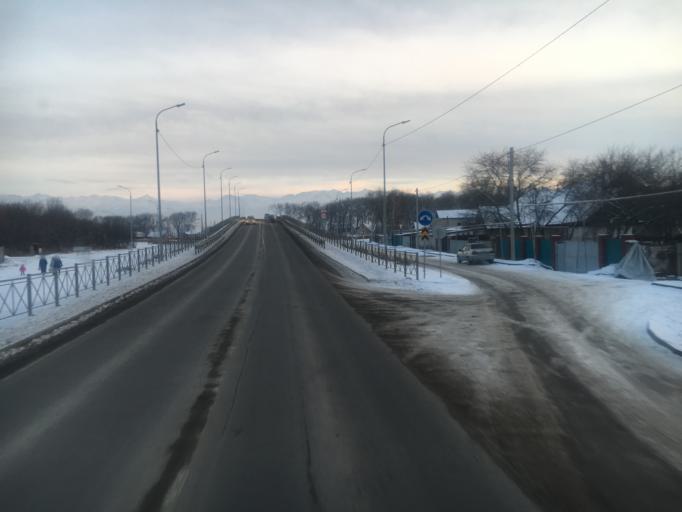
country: KZ
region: Almaty Oblysy
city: Burunday
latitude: 43.3656
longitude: 76.7250
